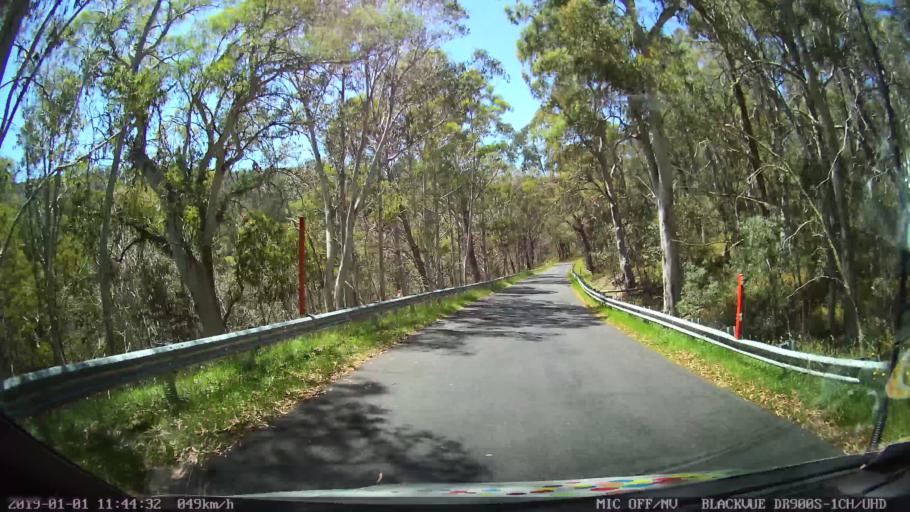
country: AU
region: New South Wales
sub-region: Snowy River
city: Jindabyne
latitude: -35.9000
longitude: 148.3934
